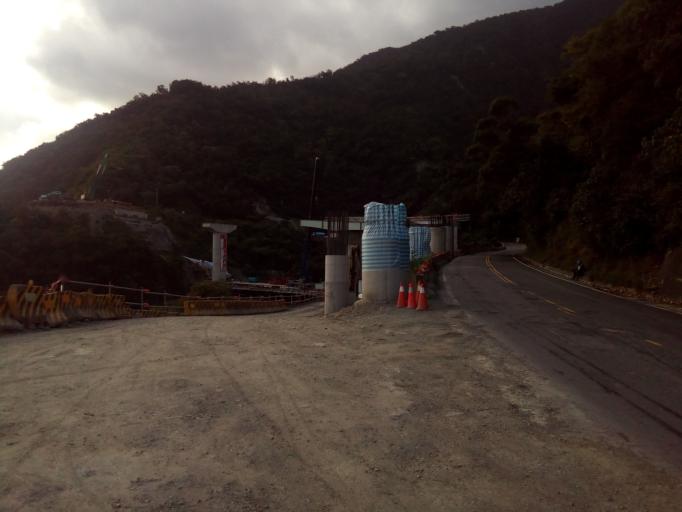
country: TW
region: Taiwan
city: Taitung City
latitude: 22.5642
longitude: 120.9798
